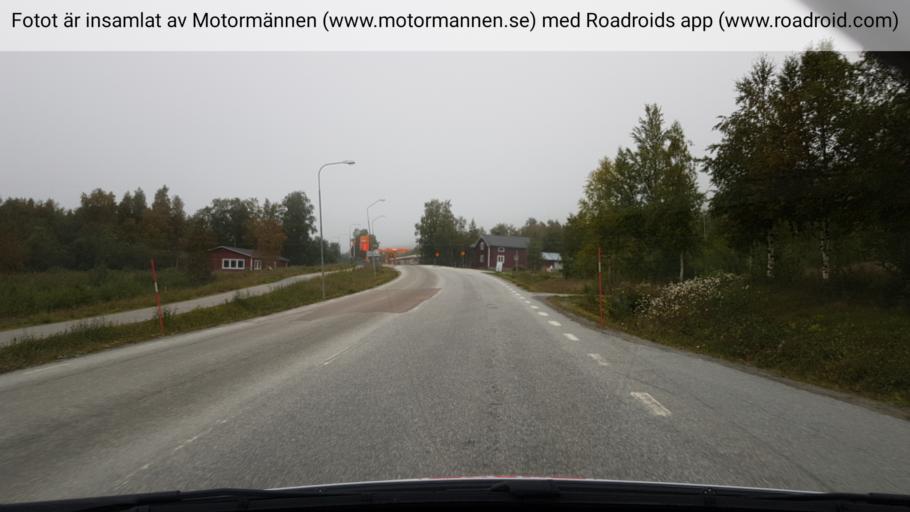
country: NO
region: Nordland
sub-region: Rana
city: Mo i Rana
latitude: 65.8166
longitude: 15.0873
